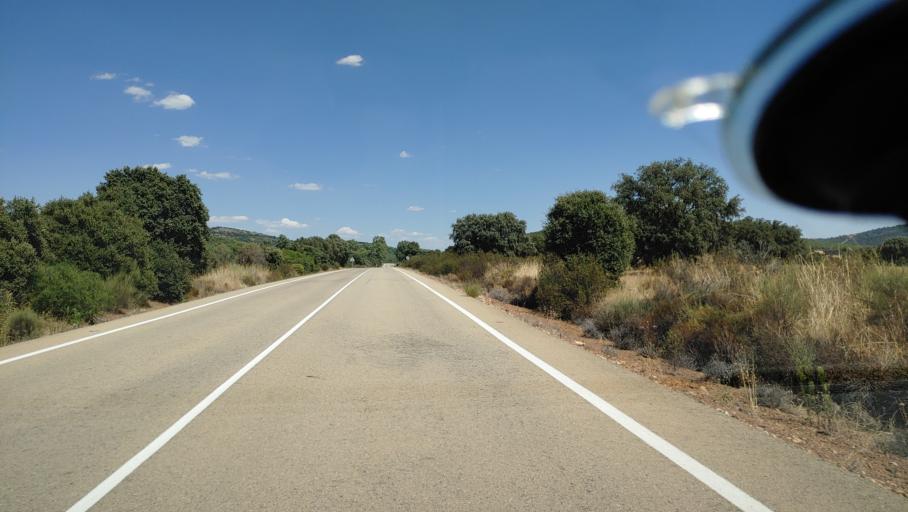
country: ES
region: Castille-La Mancha
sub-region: Provincia de Ciudad Real
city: Saceruela
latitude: 38.9821
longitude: -4.5622
